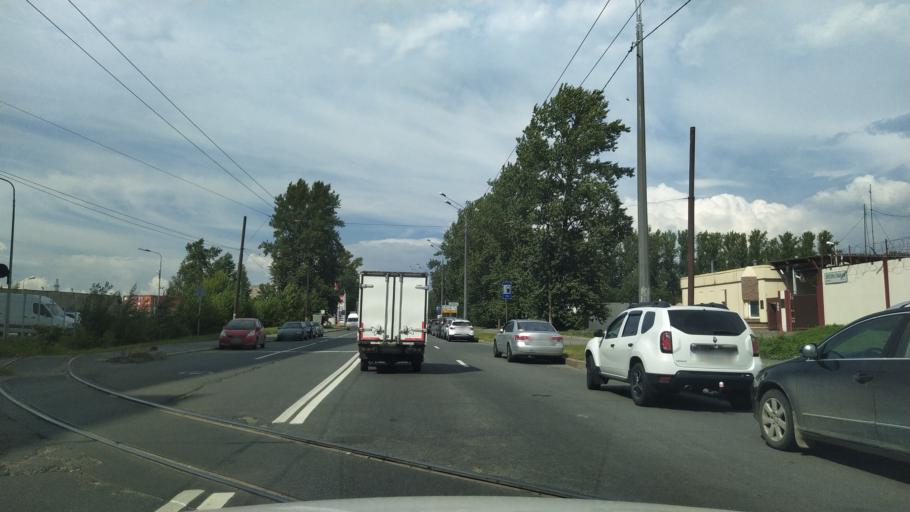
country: RU
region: Leningrad
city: Finlyandskiy
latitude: 59.9634
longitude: 30.3683
